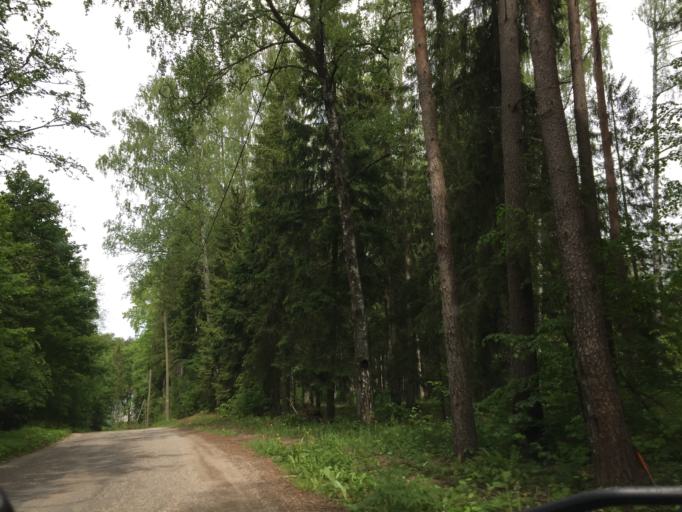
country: LV
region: Koceni
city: Koceni
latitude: 57.5039
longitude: 25.3752
